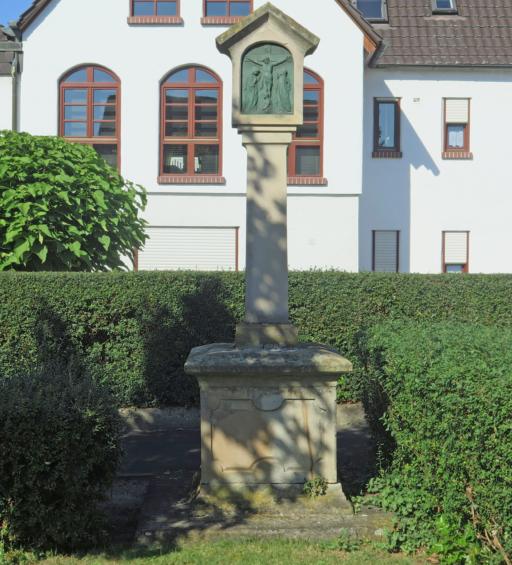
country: DE
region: Bavaria
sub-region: Regierungsbezirk Unterfranken
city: Gadheim
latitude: 50.0002
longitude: 10.3648
